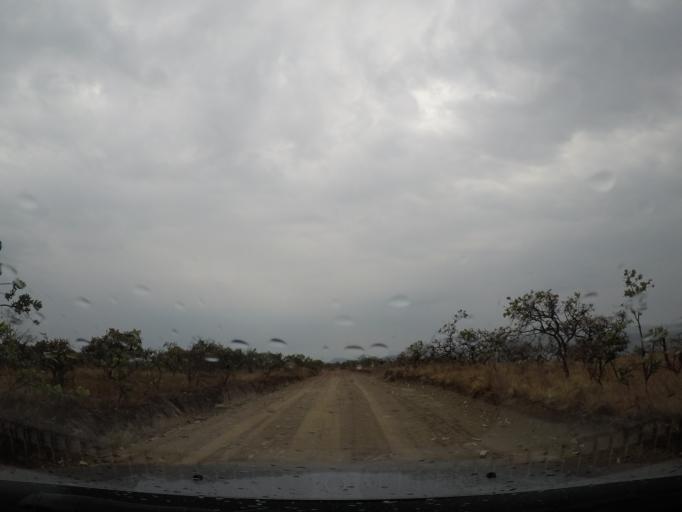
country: BR
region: Goias
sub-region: Pirenopolis
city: Pirenopolis
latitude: -15.8202
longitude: -48.9031
